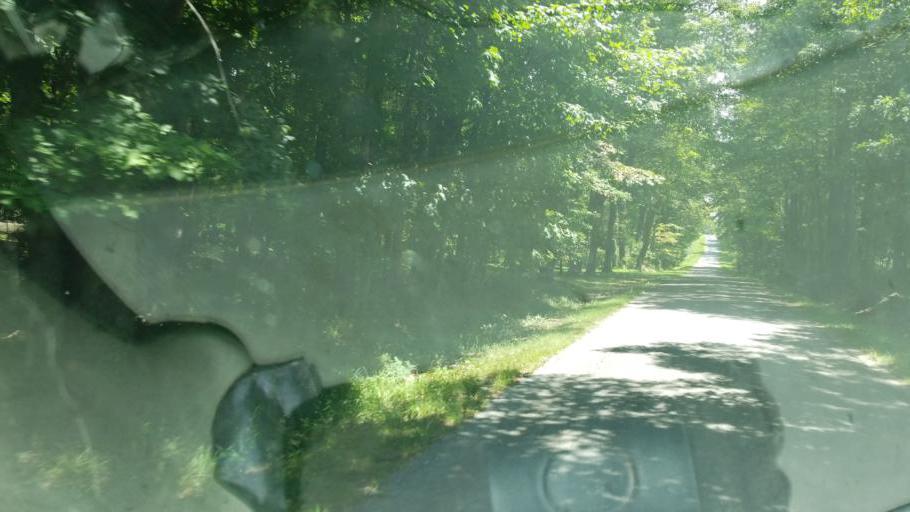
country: US
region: Ohio
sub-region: Crawford County
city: Crestline
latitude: 40.8794
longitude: -82.7795
